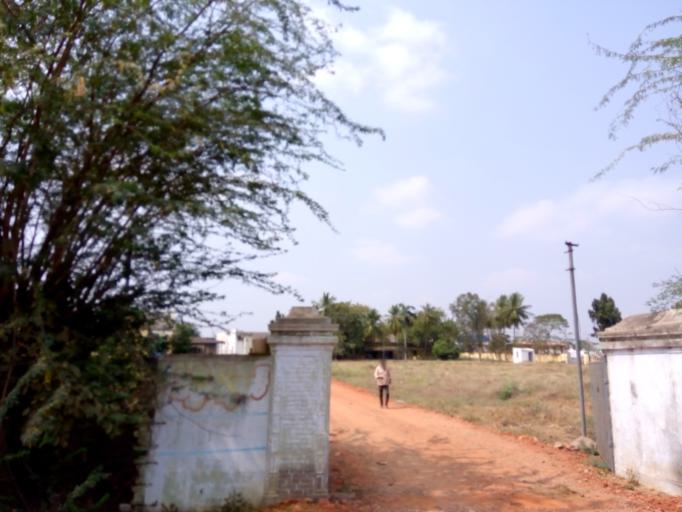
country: IN
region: Andhra Pradesh
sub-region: Prakasam
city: pedda nakkalapalem
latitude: 15.9681
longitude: 80.2727
